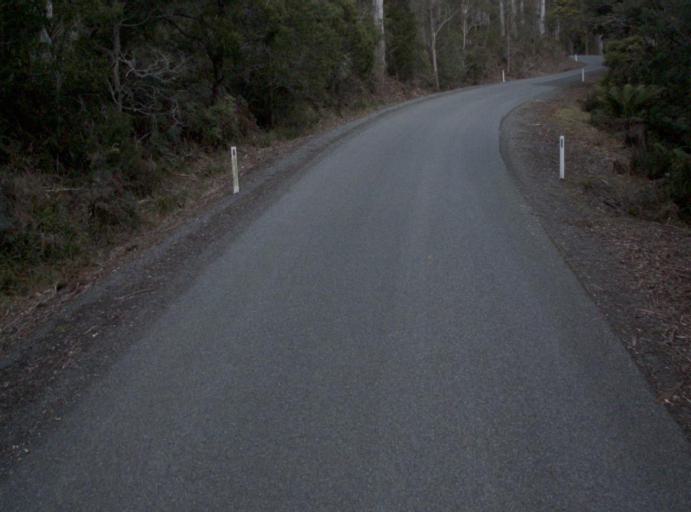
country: AU
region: Tasmania
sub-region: Launceston
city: Newstead
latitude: -41.3113
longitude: 147.3333
